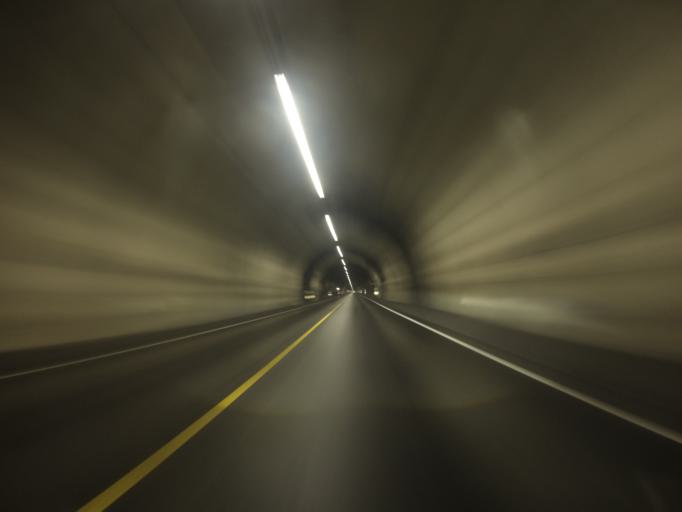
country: NO
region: Rogaland
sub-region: Suldal
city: Sand
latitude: 59.4603
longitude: 6.1779
